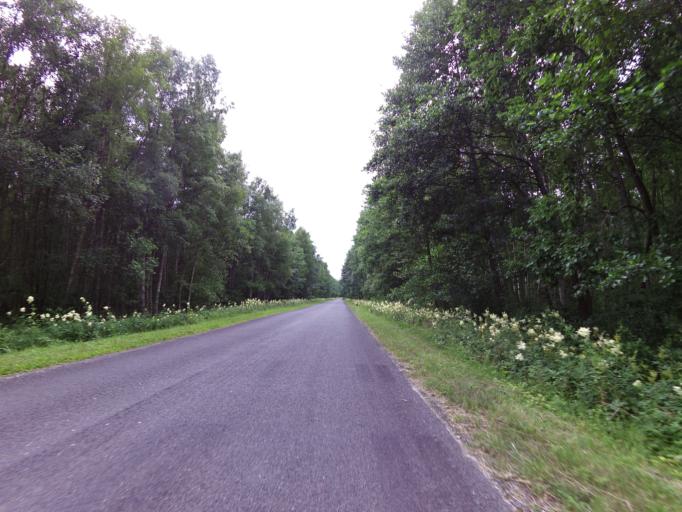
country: EE
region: Laeaene
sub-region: Vormsi vald
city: Hullo
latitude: 58.9857
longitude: 23.2687
